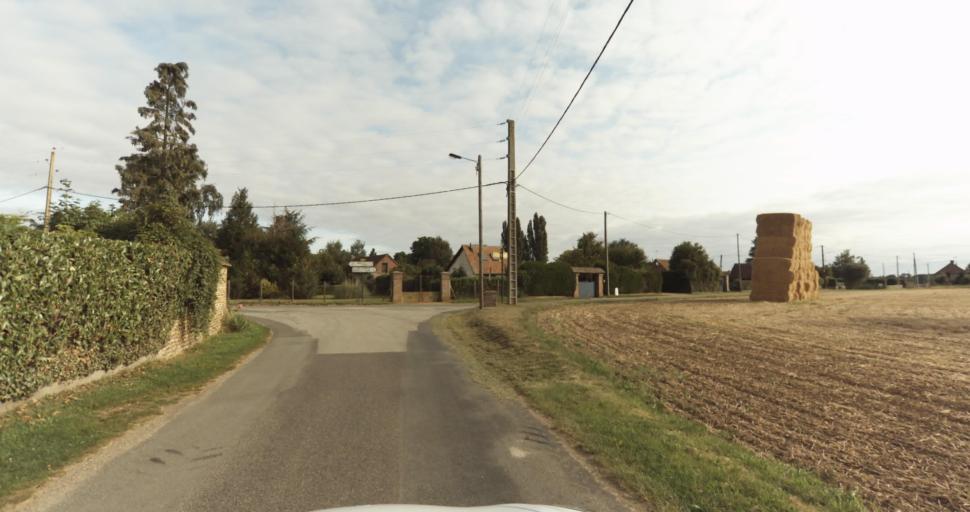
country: FR
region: Centre
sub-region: Departement d'Eure-et-Loir
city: Saint-Remy-sur-Avre
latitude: 48.8178
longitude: 1.2411
